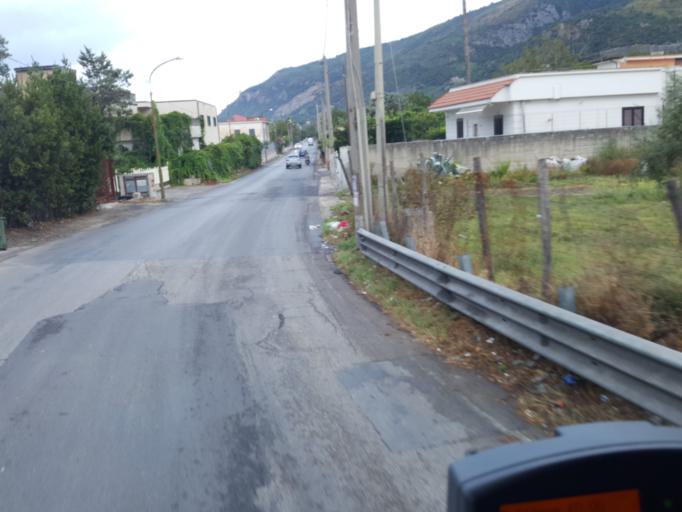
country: IT
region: Campania
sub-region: Provincia di Napoli
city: Striano
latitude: 40.8239
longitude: 14.5987
